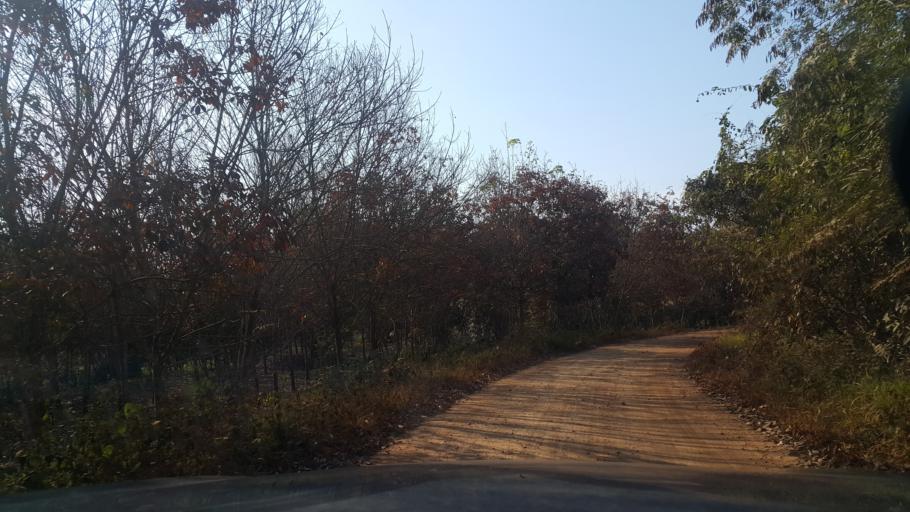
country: TH
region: Loei
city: Chiang Khan
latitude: 17.8170
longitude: 101.6169
